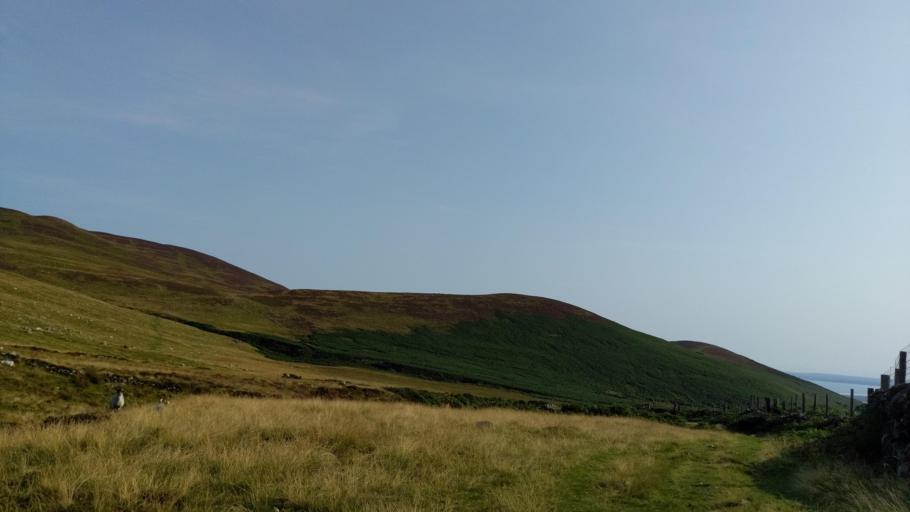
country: GB
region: Northern Ireland
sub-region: Down District
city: Warrenpoint
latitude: 54.0656
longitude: -6.3237
